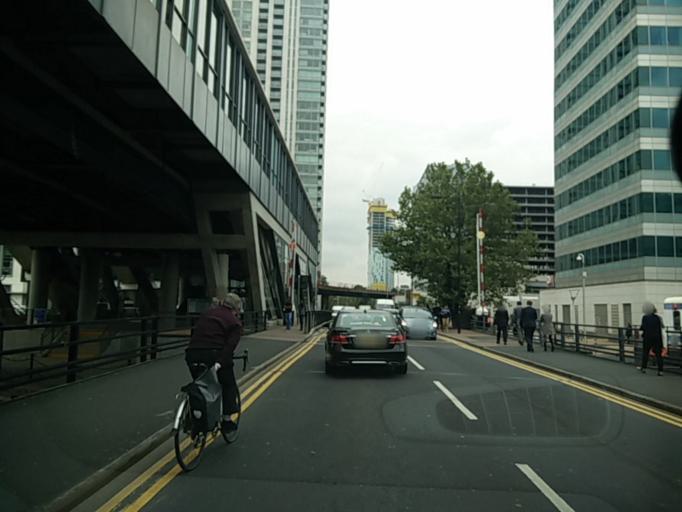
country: GB
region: England
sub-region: Greater London
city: Poplar
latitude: 51.5001
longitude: -0.0159
